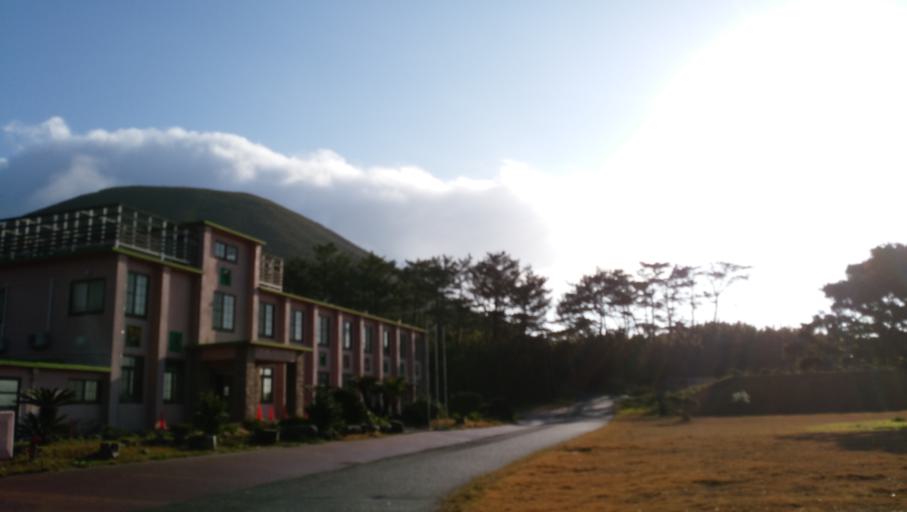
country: JP
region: Kagoshima
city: Makurazaki
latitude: 30.7803
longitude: 130.2809
